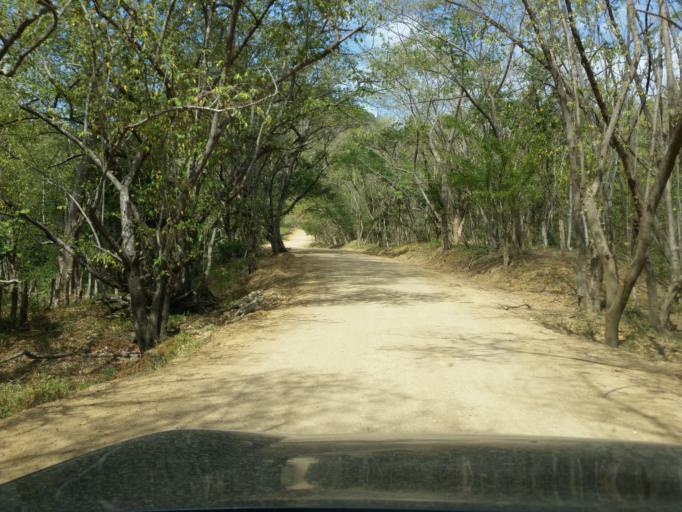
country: NI
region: Rivas
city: San Juan del Sur
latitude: 11.1484
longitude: -85.7918
